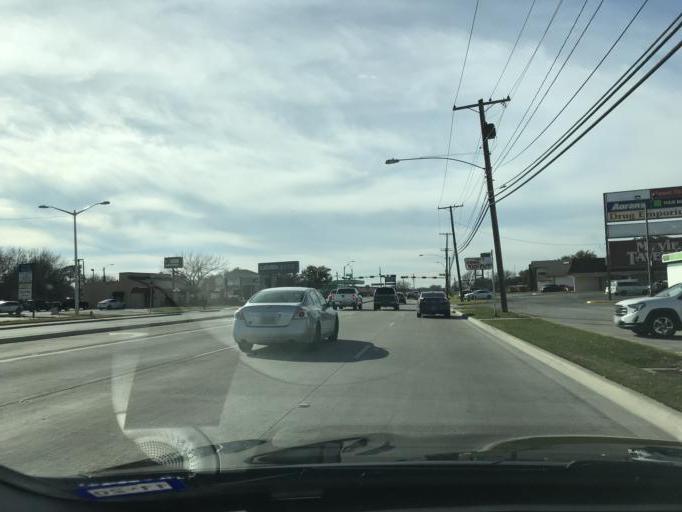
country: US
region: Texas
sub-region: Denton County
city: Denton
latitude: 33.2302
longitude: -97.1413
